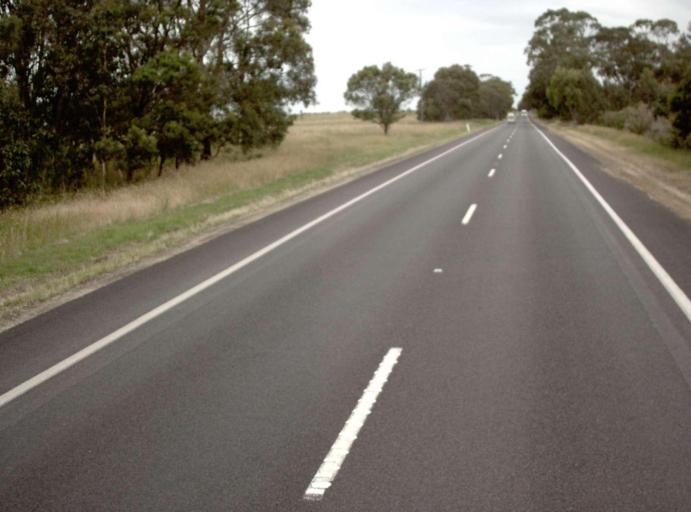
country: AU
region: Victoria
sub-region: Wellington
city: Sale
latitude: -38.3004
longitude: 147.0328
